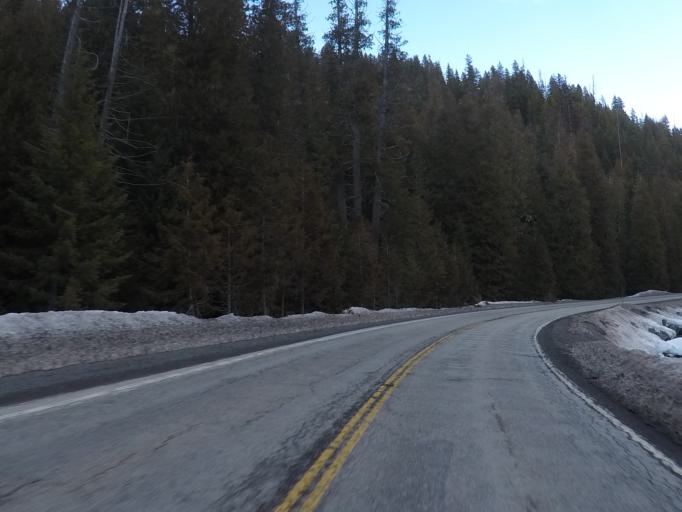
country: US
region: Montana
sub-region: Ravalli County
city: Stevensville
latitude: 46.5542
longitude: -114.6690
